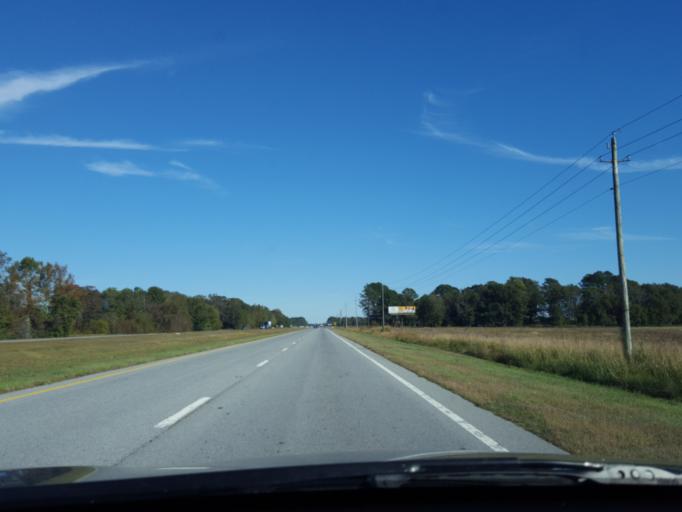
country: US
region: North Carolina
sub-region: Pitt County
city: Greenville
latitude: 35.6257
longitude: -77.3048
